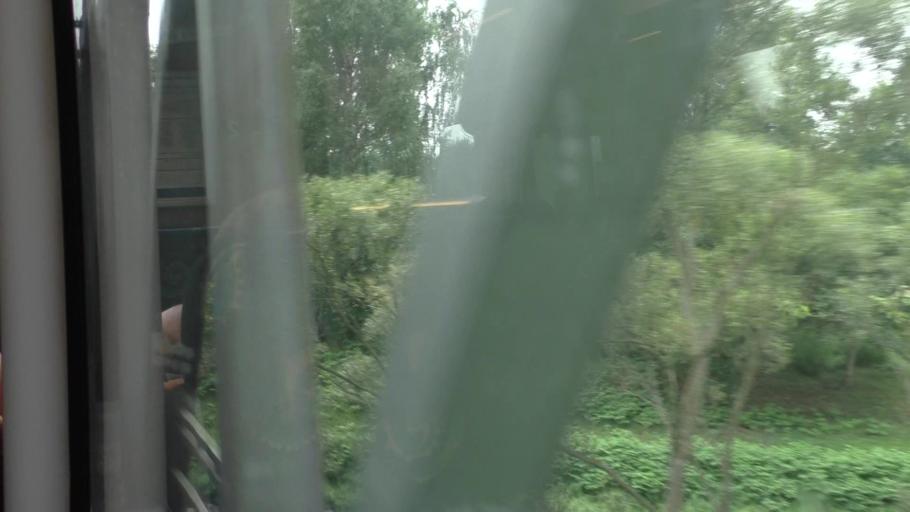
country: DE
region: Saxony
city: Hirschfelde
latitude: 50.9488
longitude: 14.8939
